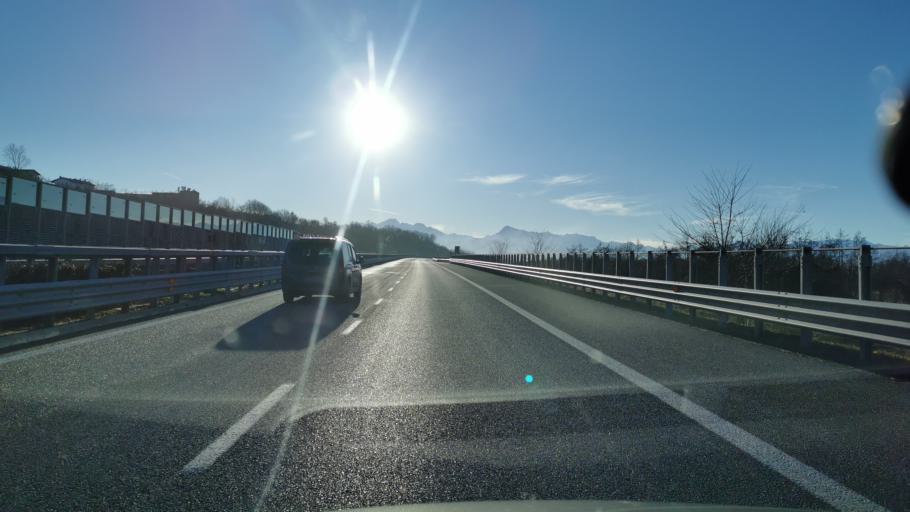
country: IT
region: Piedmont
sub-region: Provincia di Cuneo
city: Castelletto Stura
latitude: 44.4464
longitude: 7.6357
